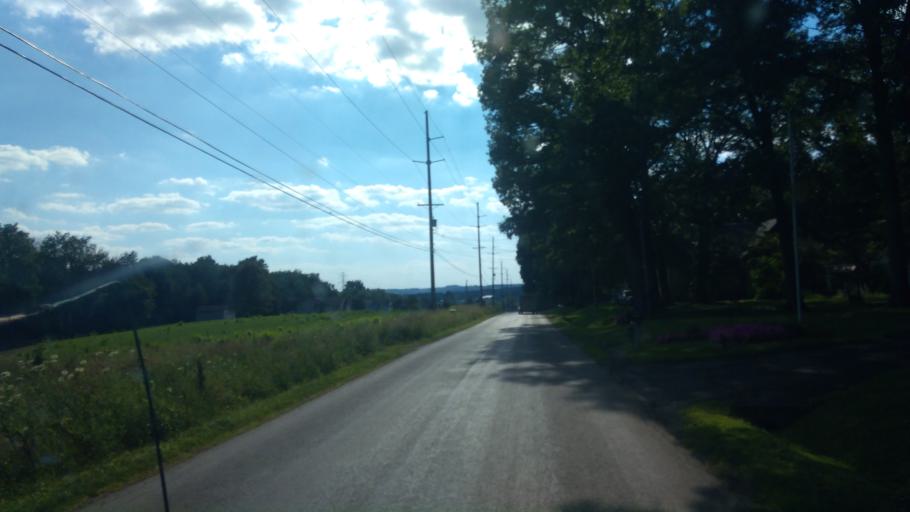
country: US
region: Ohio
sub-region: Wayne County
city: Shreve
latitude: 40.7117
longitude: -81.9511
